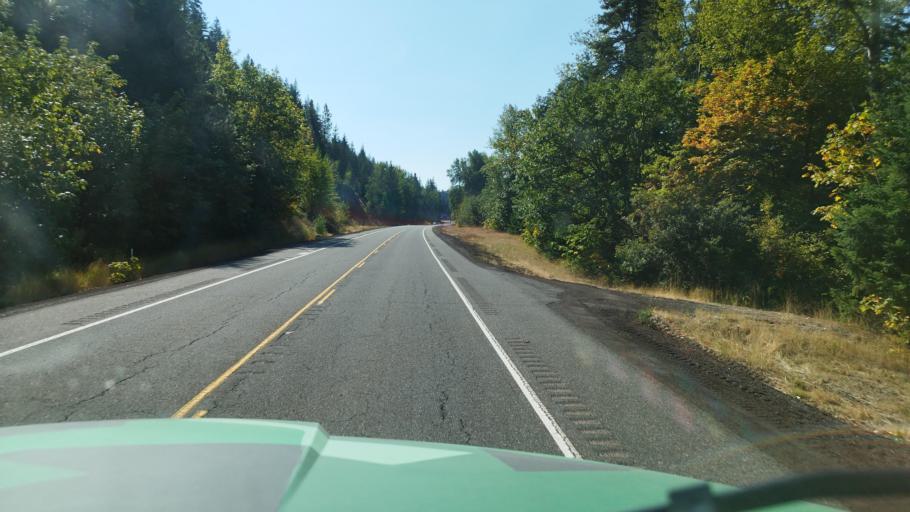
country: US
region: Oregon
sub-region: Hood River County
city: Odell
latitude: 45.5010
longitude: -121.5619
